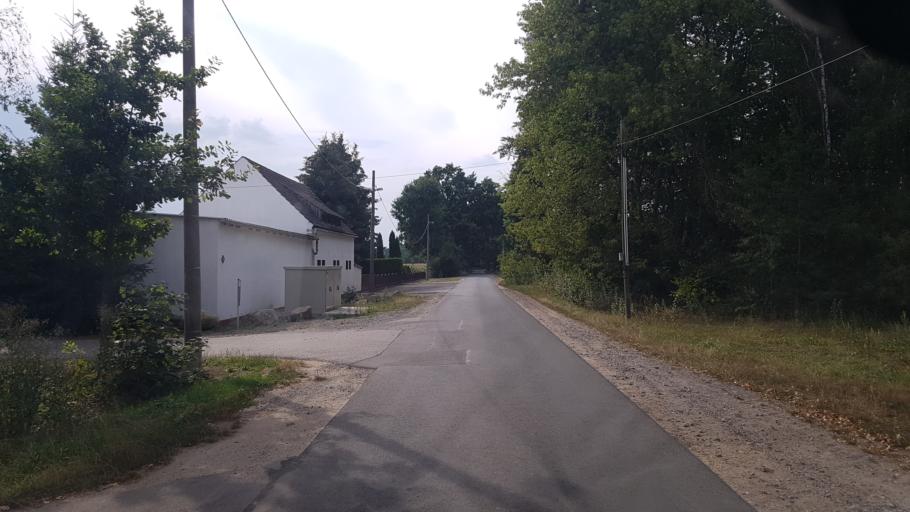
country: DE
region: Brandenburg
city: Plessa
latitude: 51.4430
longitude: 13.5827
